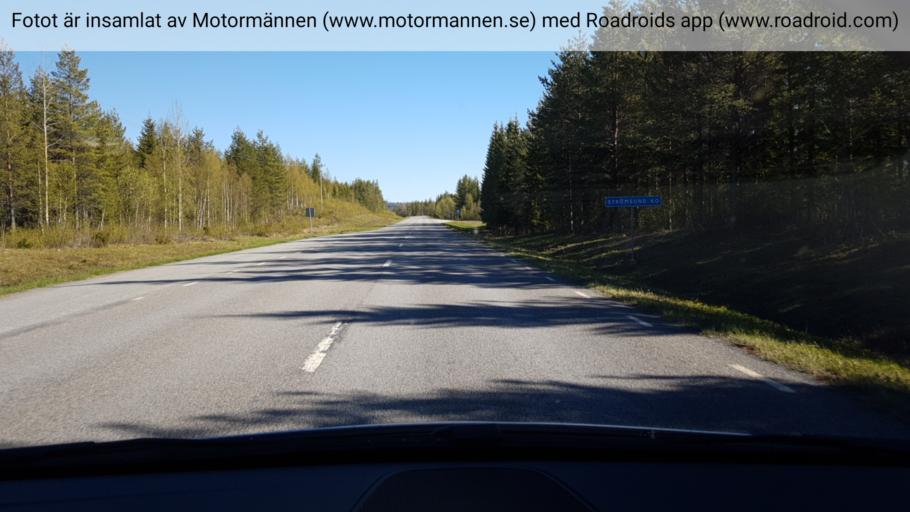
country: SE
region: Jaemtland
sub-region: Stroemsunds Kommun
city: Stroemsund
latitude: 64.2638
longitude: 15.3948
